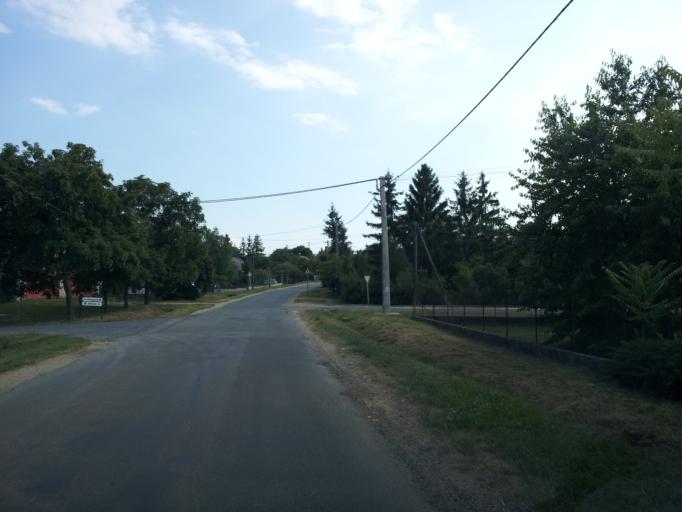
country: HU
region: Veszprem
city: Zanka
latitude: 46.9808
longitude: 17.6927
